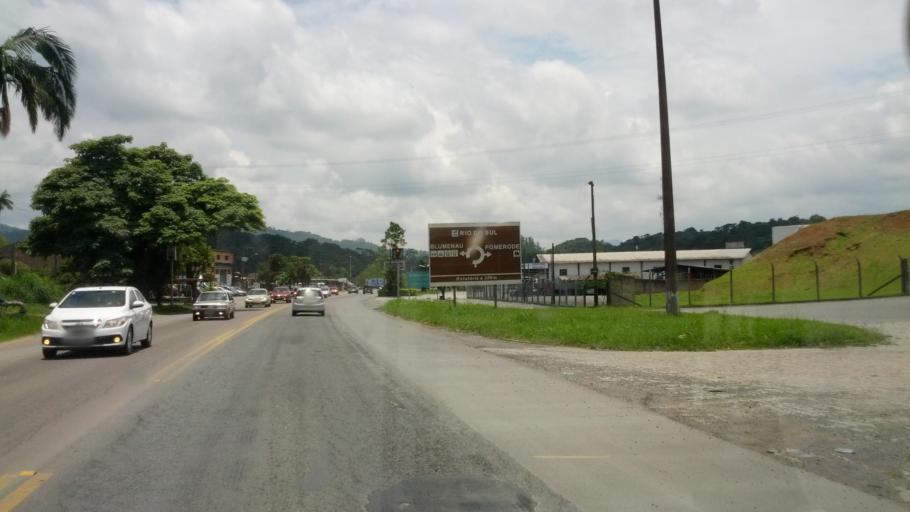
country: BR
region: Santa Catarina
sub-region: Blumenau
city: Blumenau
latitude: -26.8812
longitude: -49.1377
